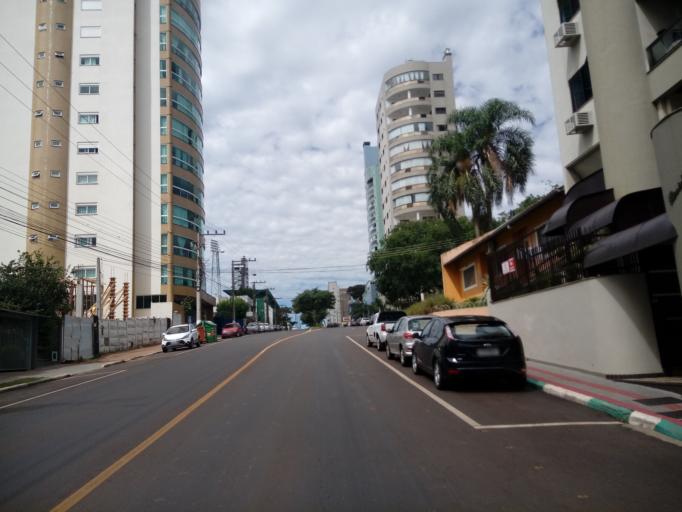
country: BR
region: Santa Catarina
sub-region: Chapeco
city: Chapeco
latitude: -27.1020
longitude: -52.6084
